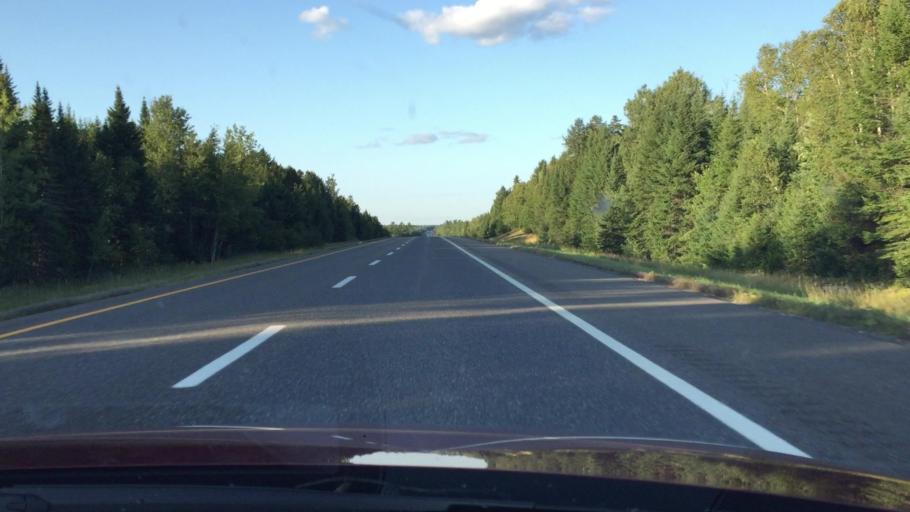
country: US
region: Maine
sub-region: Penobscot County
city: Patten
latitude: 46.0588
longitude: -68.2346
